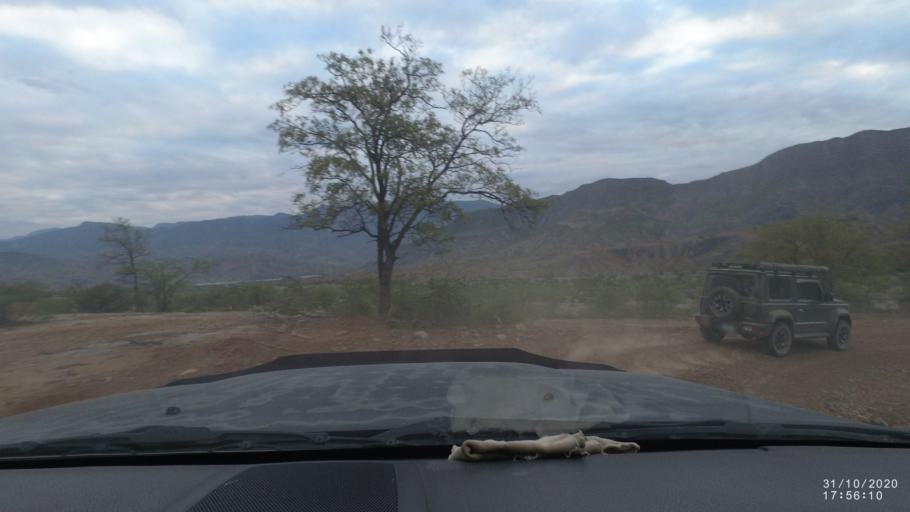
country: BO
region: Chuquisaca
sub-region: Provincia Zudanez
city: Mojocoya
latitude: -18.6491
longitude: -64.5291
